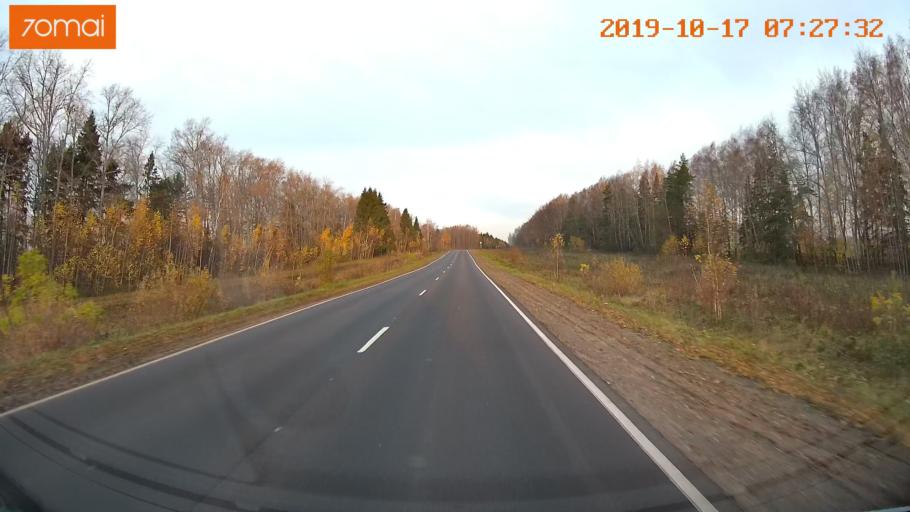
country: RU
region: Ivanovo
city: Gavrilov Posad
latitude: 56.3623
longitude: 40.0738
